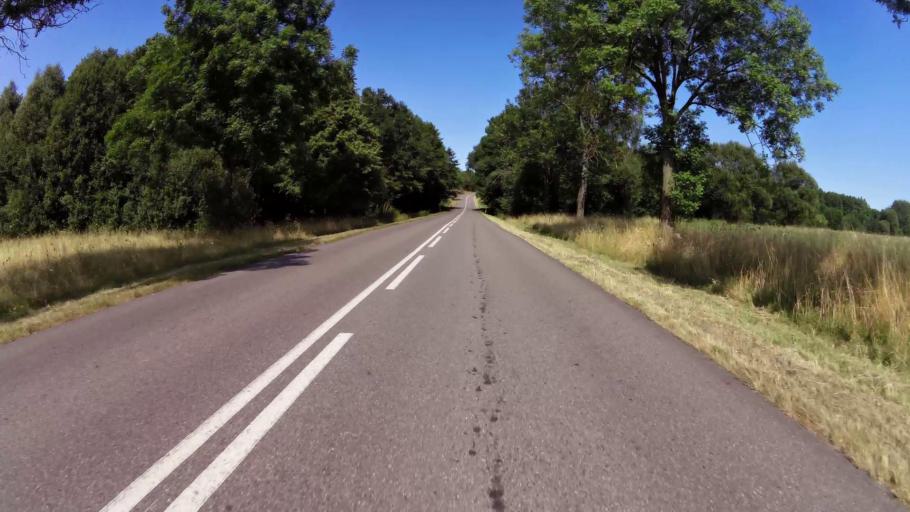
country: PL
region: West Pomeranian Voivodeship
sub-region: Powiat stargardzki
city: Suchan
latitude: 53.2978
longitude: 15.3660
